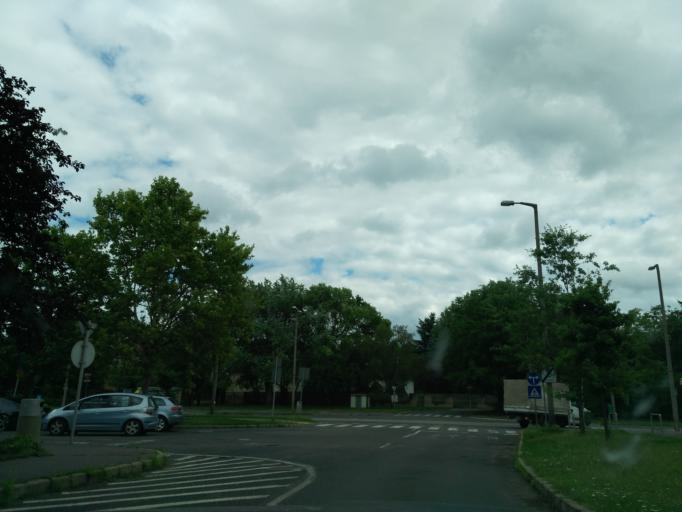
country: HU
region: Hajdu-Bihar
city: Debrecen
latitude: 47.5459
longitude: 21.6211
